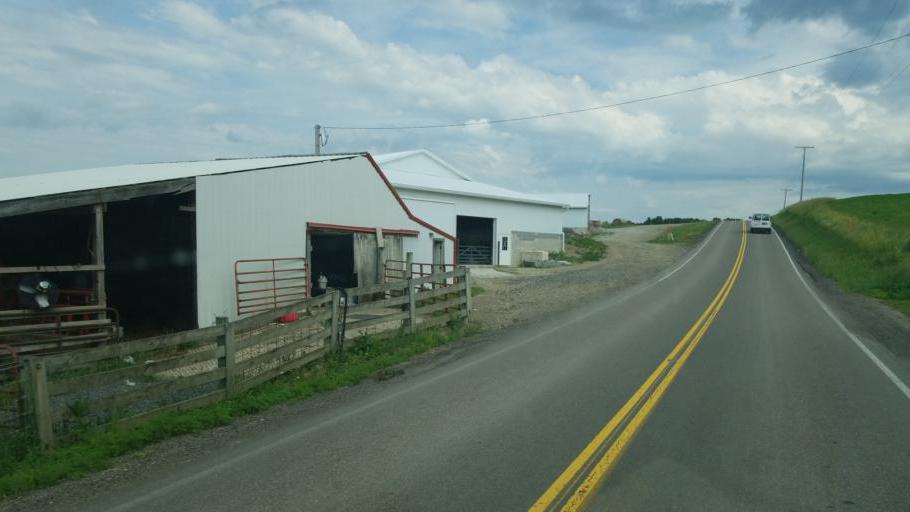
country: US
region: Ohio
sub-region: Knox County
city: Danville
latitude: 40.4595
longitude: -82.2640
